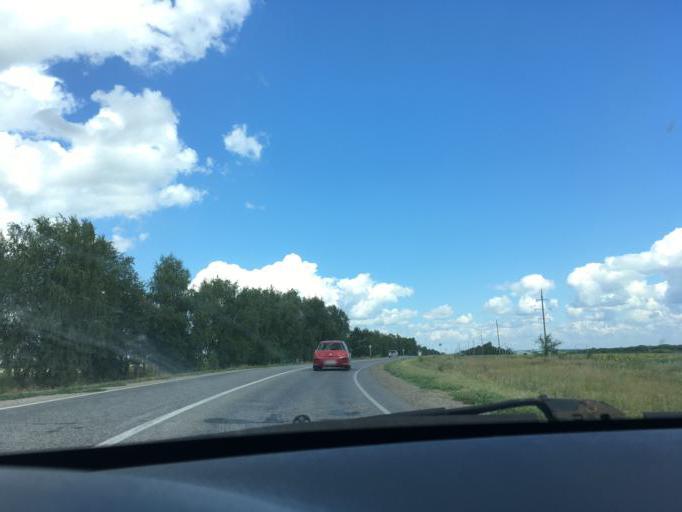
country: RU
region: Samara
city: Bezenchuk
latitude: 53.0397
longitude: 49.4412
